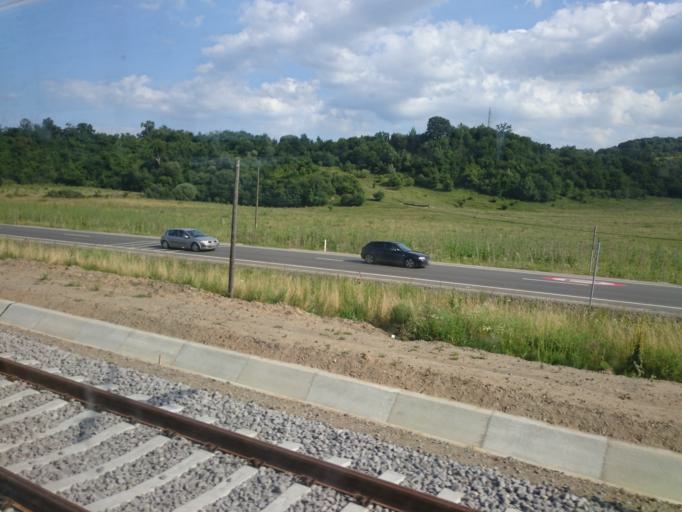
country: RO
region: Sibiu
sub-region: Comuna Hoghilag
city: Hoghilag
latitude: 46.2202
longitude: 24.6208
